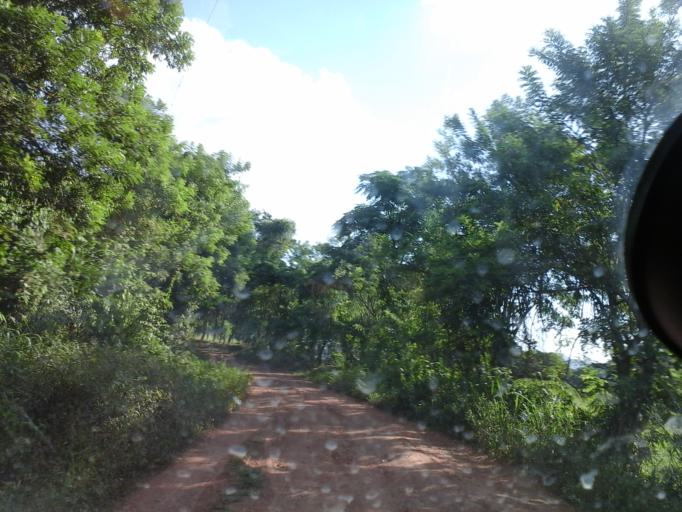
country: CO
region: Cesar
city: San Diego
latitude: 10.2478
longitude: -73.1183
